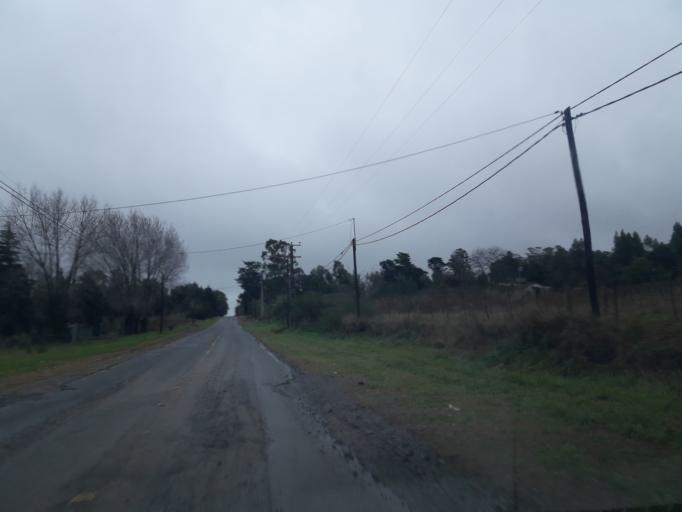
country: AR
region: Buenos Aires
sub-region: Partido de Tandil
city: Tandil
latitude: -37.3279
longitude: -59.1748
